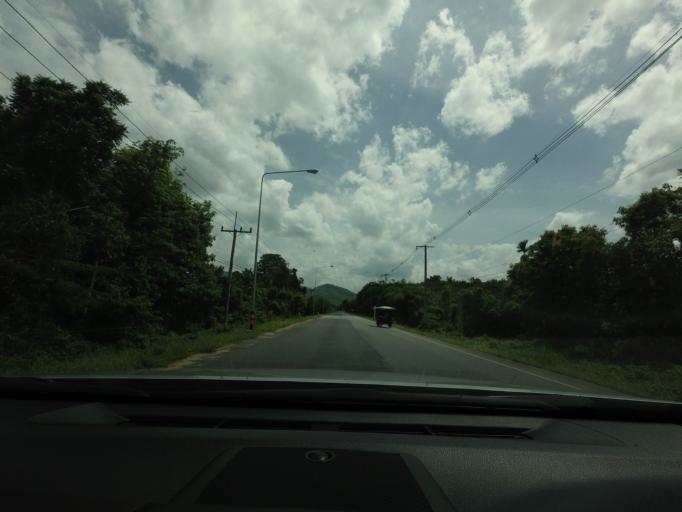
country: TH
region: Yala
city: Raman
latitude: 6.4576
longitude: 101.3626
